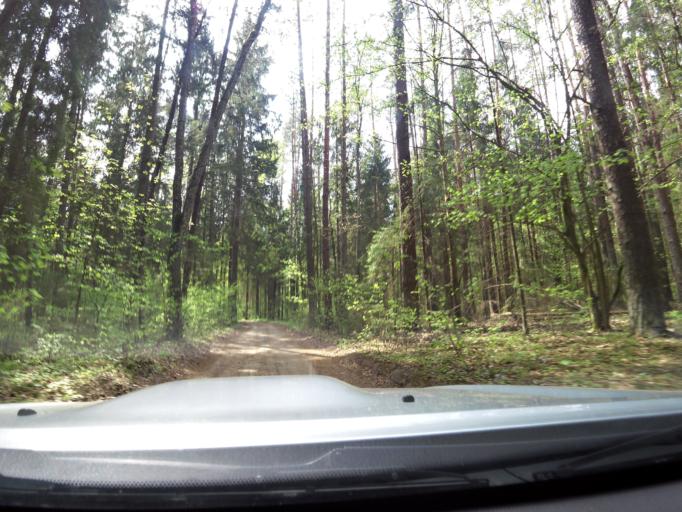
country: LT
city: Salcininkai
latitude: 54.4260
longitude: 25.3085
